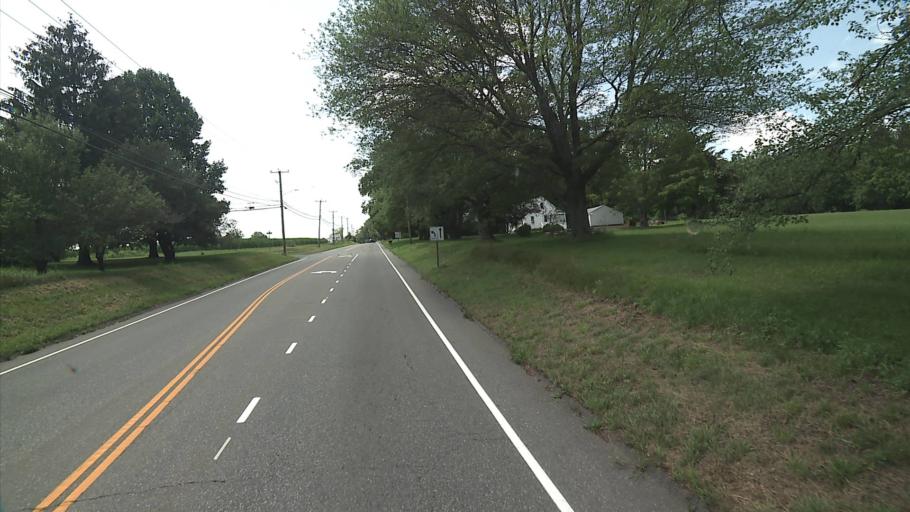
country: US
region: Connecticut
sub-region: Tolland County
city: Coventry Lake
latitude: 41.7984
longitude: -72.3820
